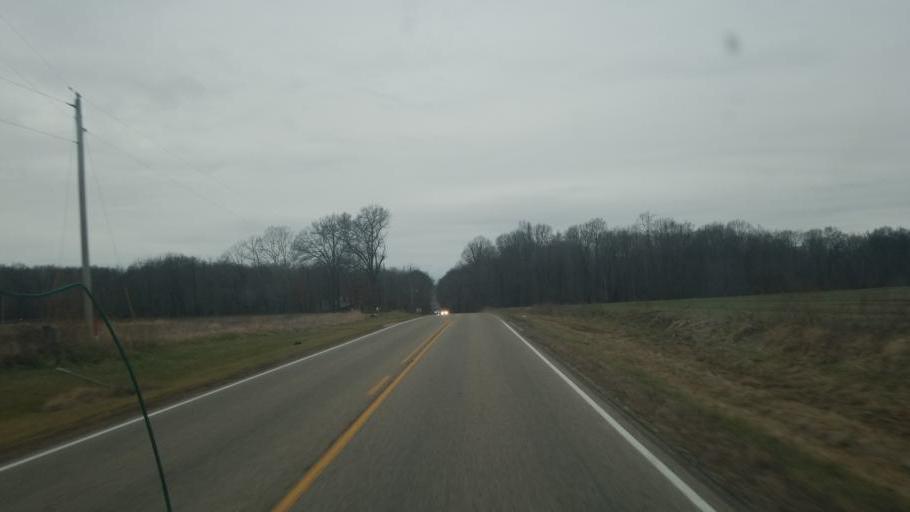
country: US
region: Indiana
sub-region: Clay County
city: Middlebury
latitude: 39.3629
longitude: -86.9584
